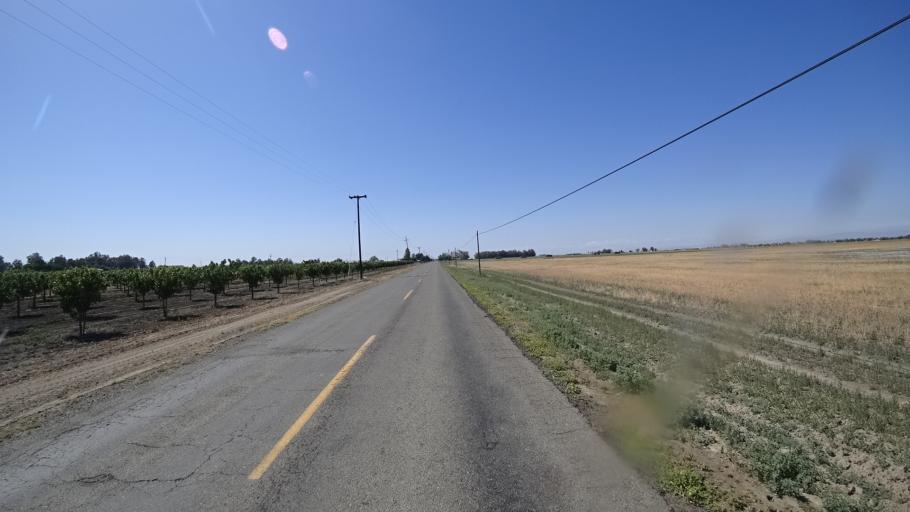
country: US
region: California
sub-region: Kings County
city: Stratford
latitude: 36.2065
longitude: -119.7982
